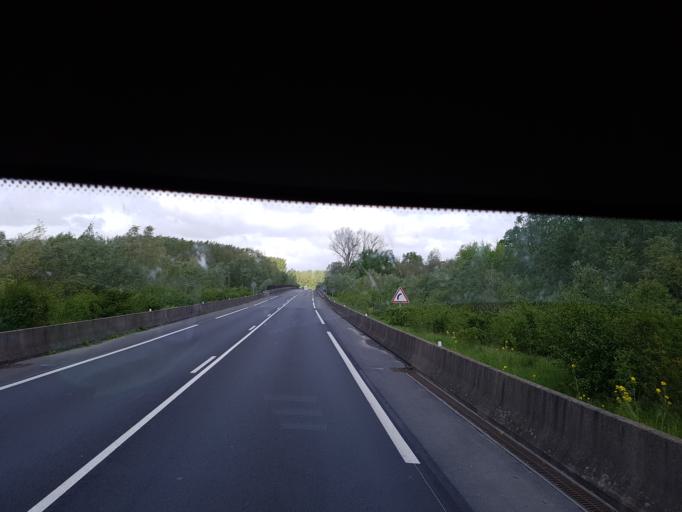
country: FR
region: Nord-Pas-de-Calais
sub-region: Departement du Nord
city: Proville
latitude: 50.1567
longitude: 3.1895
